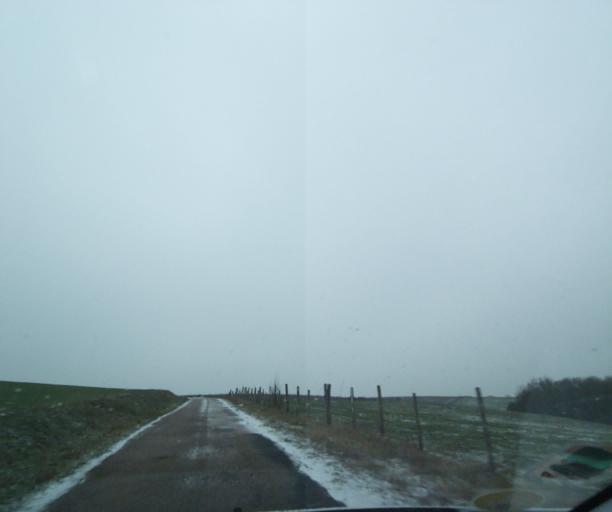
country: FR
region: Champagne-Ardenne
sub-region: Departement de la Haute-Marne
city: Wassy
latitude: 48.4663
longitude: 5.0063
